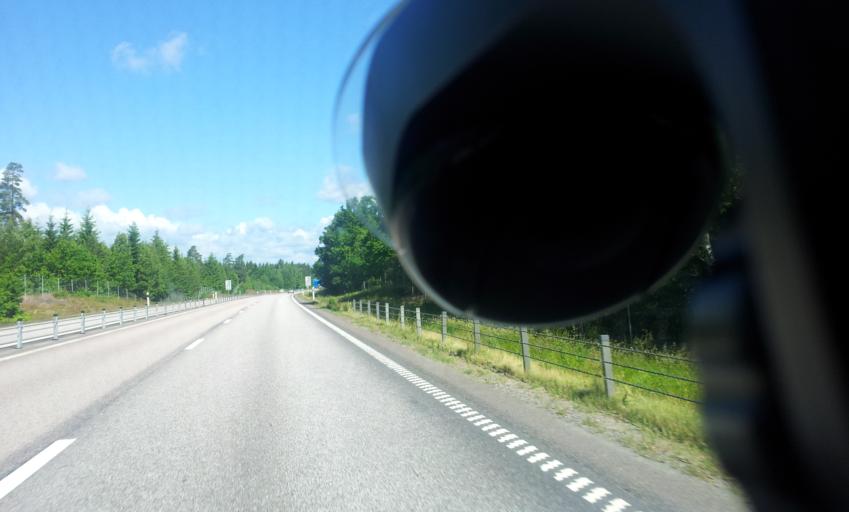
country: SE
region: Kalmar
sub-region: Oskarshamns Kommun
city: Paskallavik
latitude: 57.1886
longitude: 16.4406
